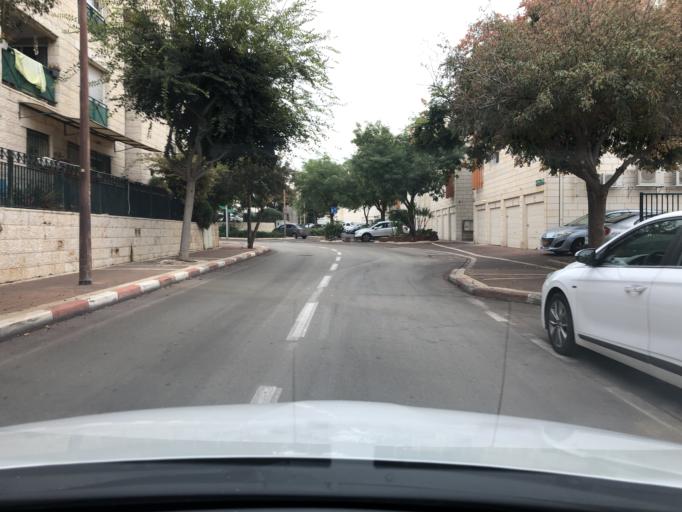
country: IL
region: Central District
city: Modiin
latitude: 31.9079
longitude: 35.0083
